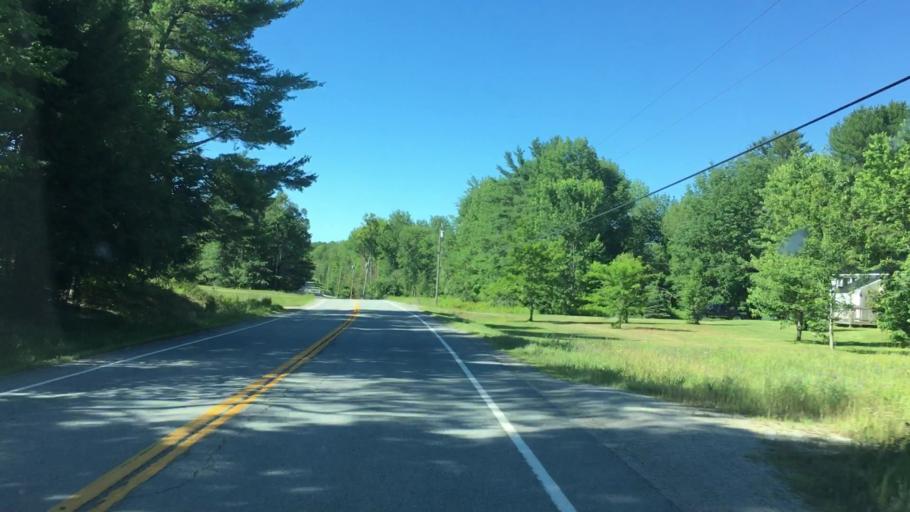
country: US
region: Maine
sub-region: Hancock County
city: Dedham
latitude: 44.6848
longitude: -68.6652
